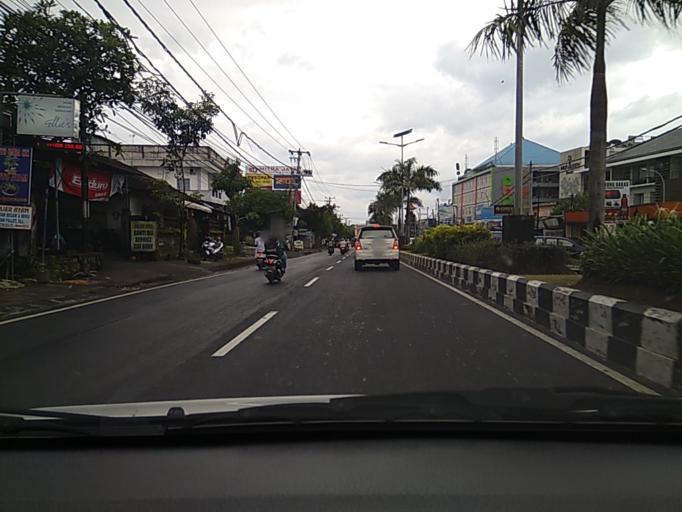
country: ID
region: Bali
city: Bualu
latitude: -8.7853
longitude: 115.1995
